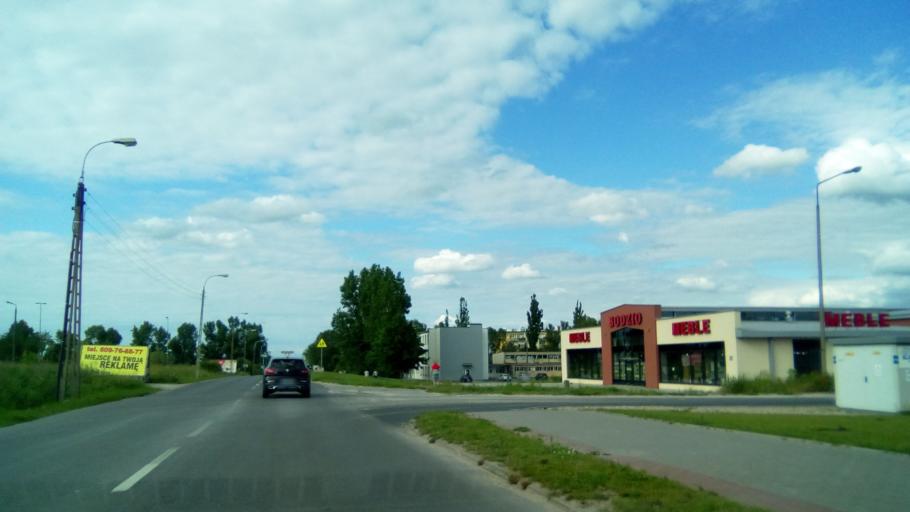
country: PL
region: Greater Poland Voivodeship
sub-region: Powiat gnieznienski
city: Gniezno
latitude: 52.5548
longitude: 17.6061
